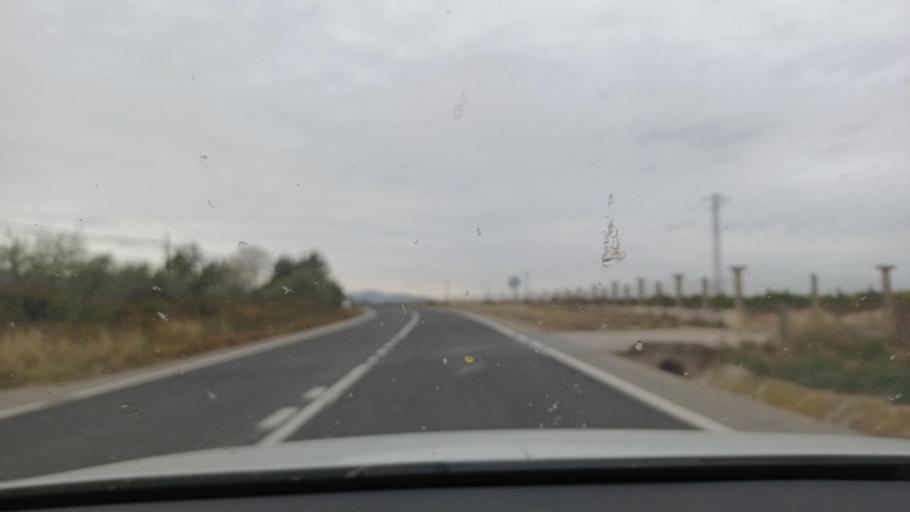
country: ES
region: Catalonia
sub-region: Provincia de Tarragona
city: Santa Barbara
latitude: 40.6987
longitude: 0.4774
